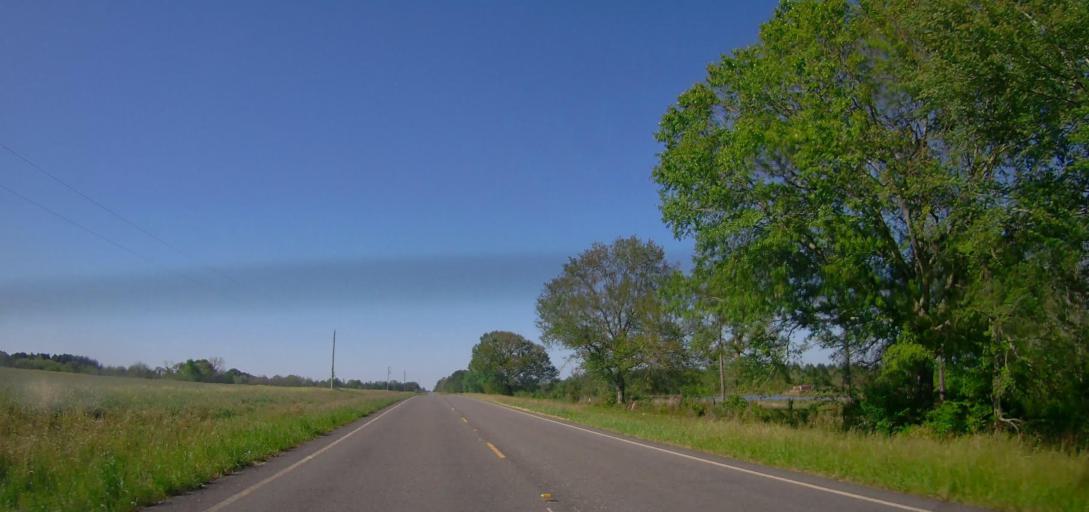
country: US
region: Georgia
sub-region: Wilcox County
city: Rochelle
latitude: 32.0525
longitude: -83.5037
